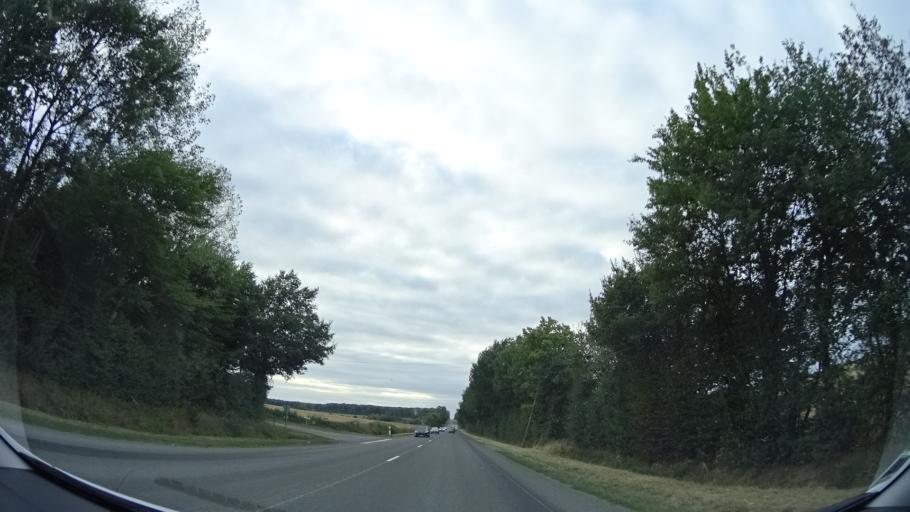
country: FR
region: Pays de la Loire
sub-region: Departement de la Sarthe
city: Bouloire
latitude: 47.9799
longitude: 0.5225
